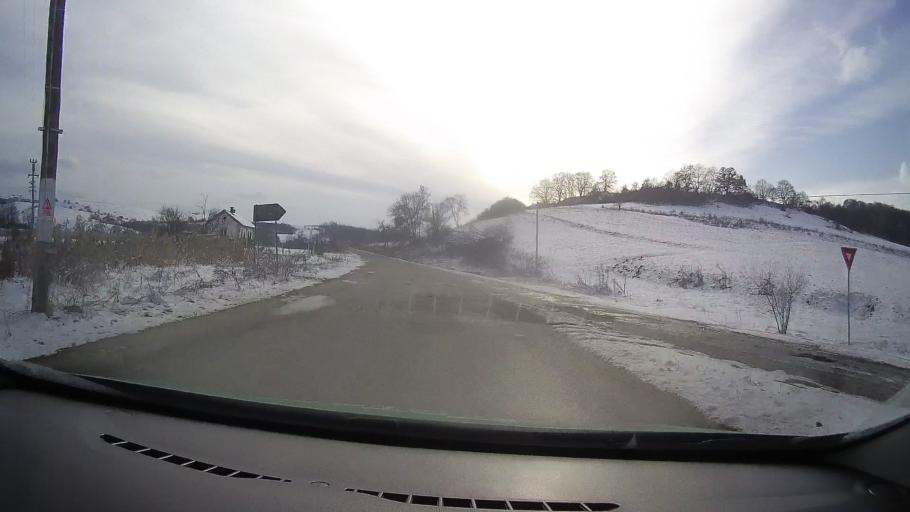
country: RO
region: Sibiu
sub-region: Comuna Iacobeni
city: Iacobeni
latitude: 46.0197
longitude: 24.6966
